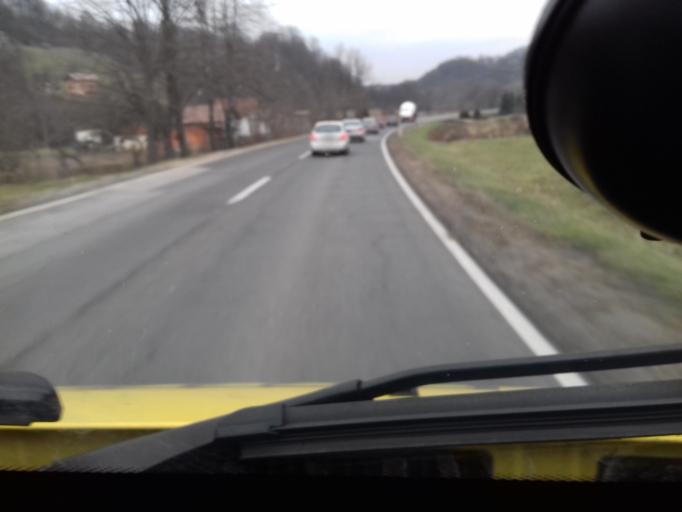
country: BA
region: Federation of Bosnia and Herzegovina
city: Lijesnica
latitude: 44.5034
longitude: 18.0795
